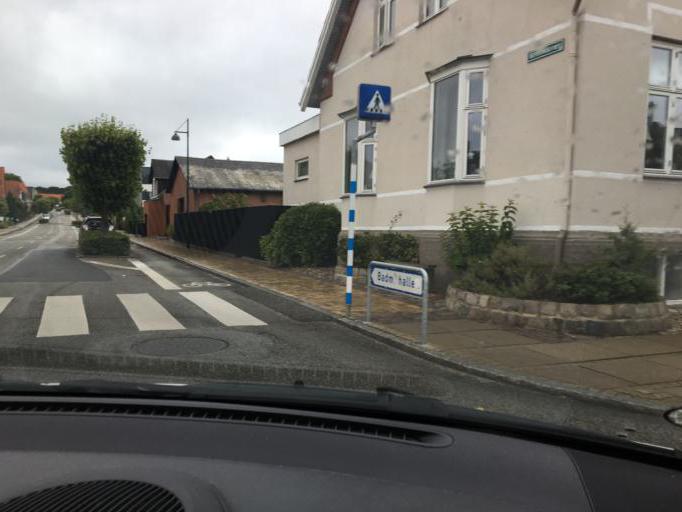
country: DK
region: South Denmark
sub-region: Middelfart Kommune
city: Middelfart
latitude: 55.5030
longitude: 9.7275
